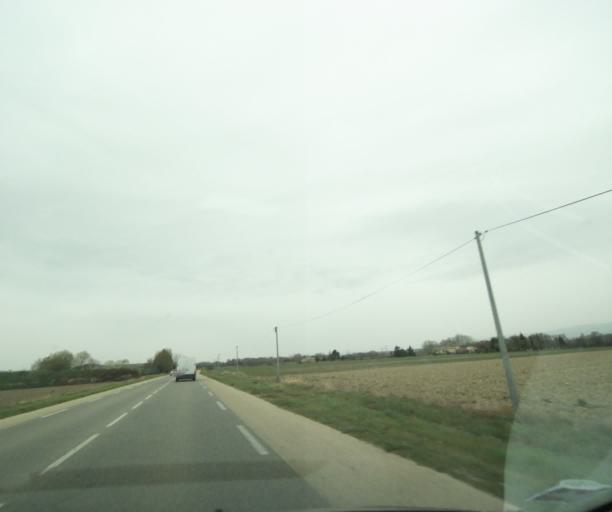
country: FR
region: Provence-Alpes-Cote d'Azur
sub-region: Departement des Bouches-du-Rhone
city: Peyrolles-en-Provence
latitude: 43.6471
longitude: 5.5592
